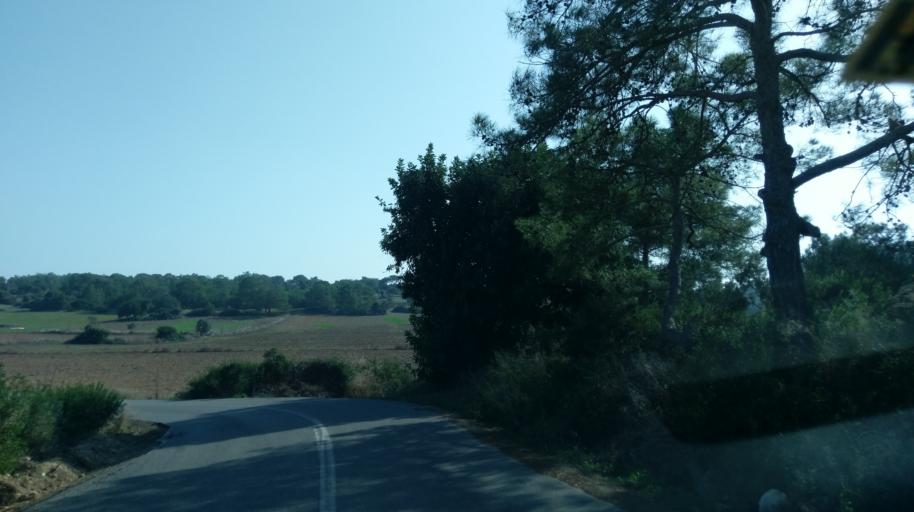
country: CY
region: Ammochostos
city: Leonarisso
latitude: 35.4768
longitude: 34.1925
